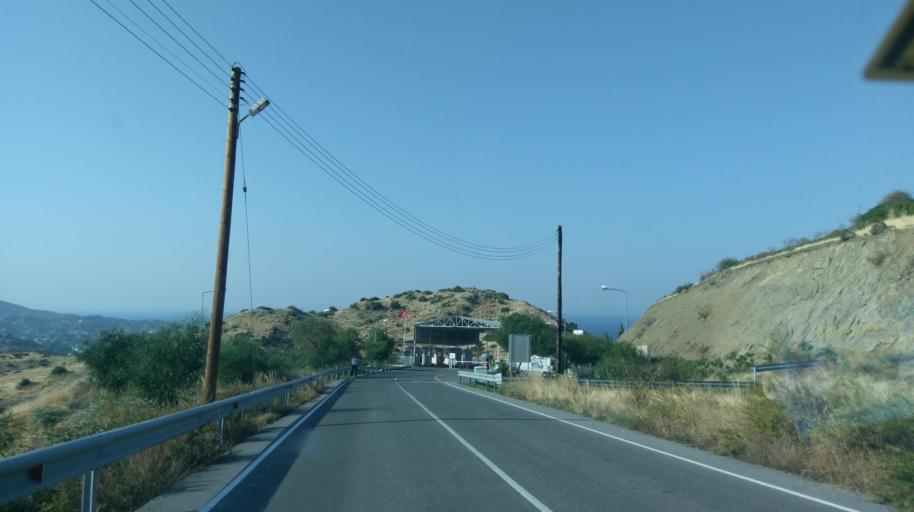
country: CY
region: Lefkosia
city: Kato Pyrgos
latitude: 35.1696
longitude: 32.7074
